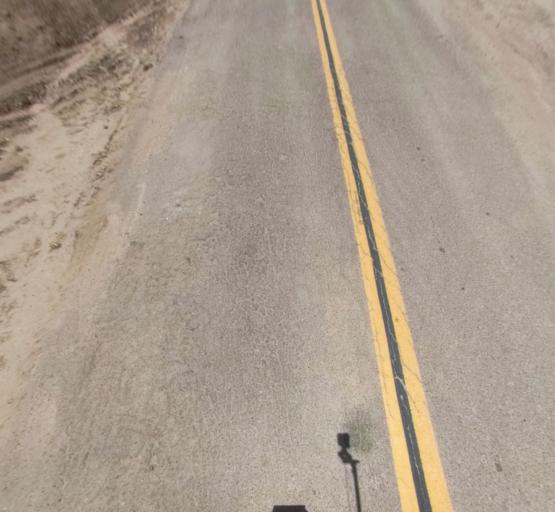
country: US
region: California
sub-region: Madera County
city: Parkwood
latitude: 36.9165
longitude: -120.0928
